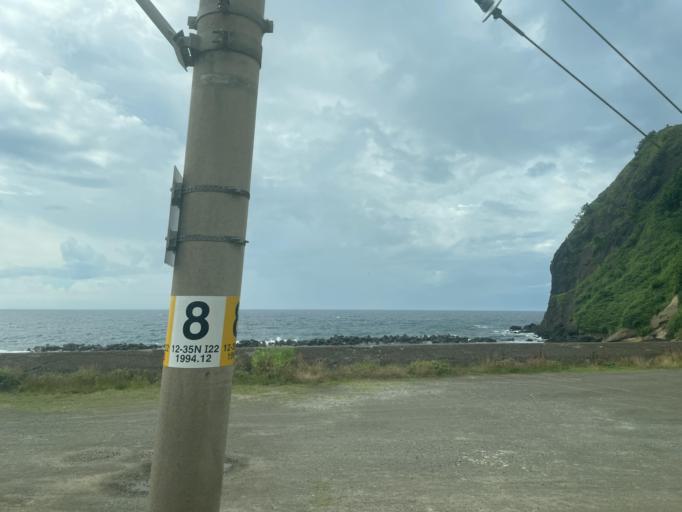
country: JP
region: Niigata
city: Kashiwazaki
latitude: 37.3220
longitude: 138.4372
